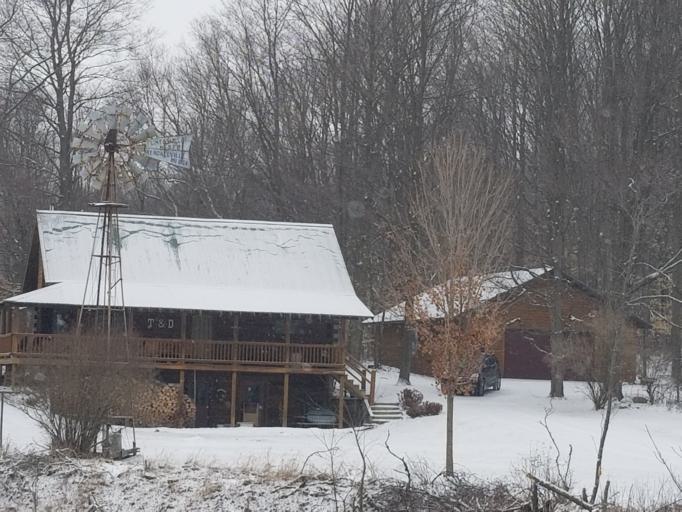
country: US
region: Michigan
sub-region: Osceola County
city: Evart
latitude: 44.1033
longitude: -85.2094
